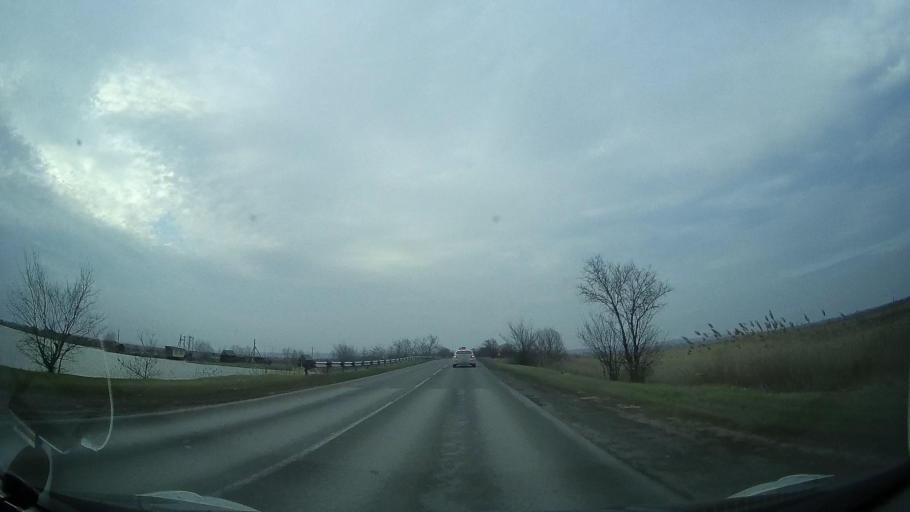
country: RU
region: Rostov
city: Ol'ginskaya
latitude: 47.2039
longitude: 39.9285
